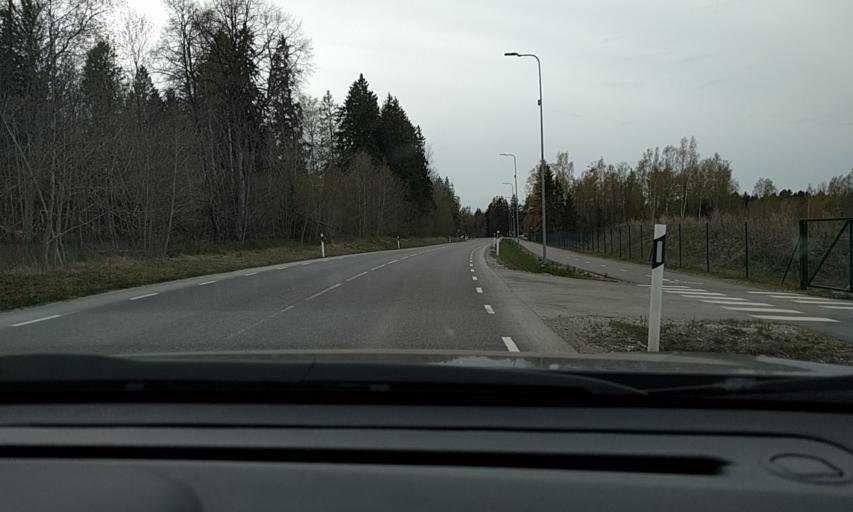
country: EE
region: Harju
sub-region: Viimsi vald
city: Viimsi
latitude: 59.5278
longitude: 24.8795
